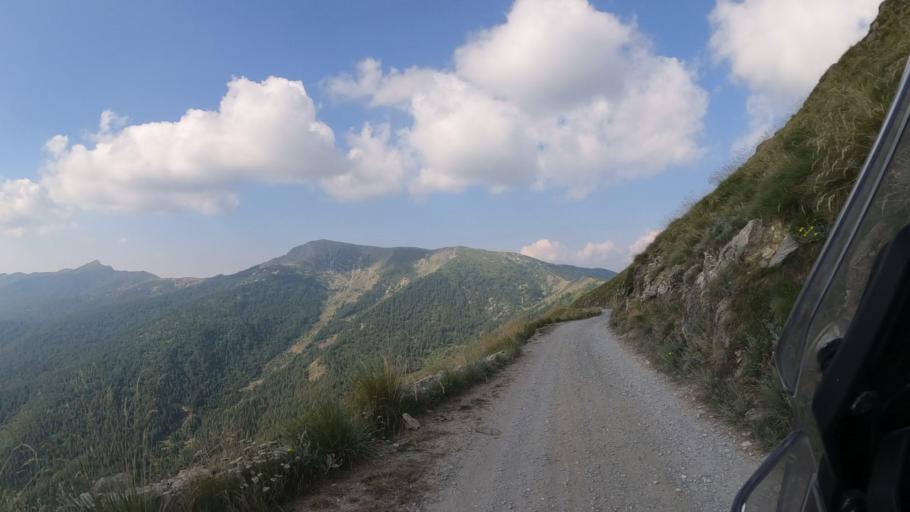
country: IT
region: Piedmont
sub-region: Provincia di Cuneo
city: Briga Alta
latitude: 44.1468
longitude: 7.6944
